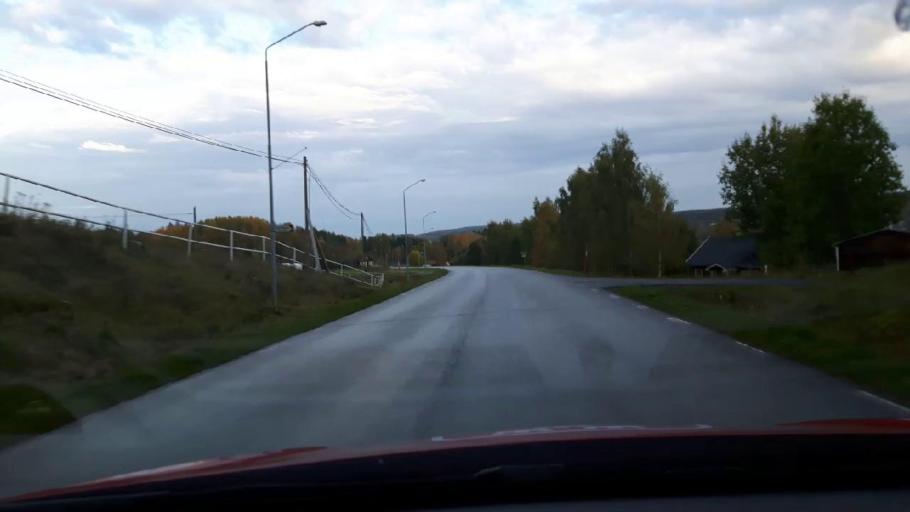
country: SE
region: Jaemtland
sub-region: OEstersunds Kommun
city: Lit
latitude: 63.3179
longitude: 14.8262
